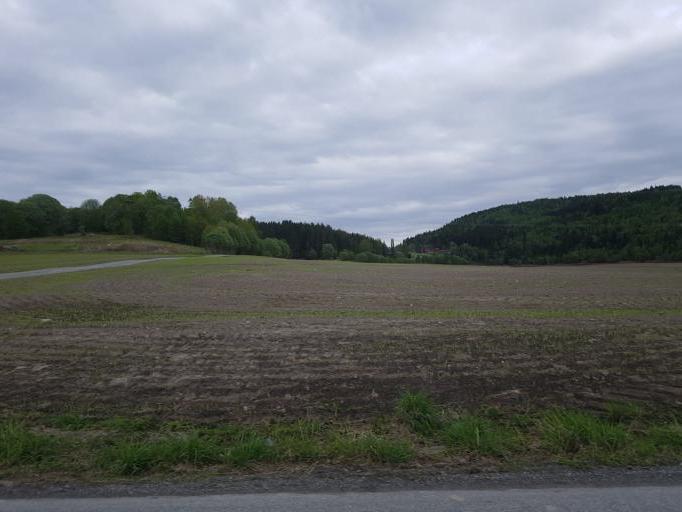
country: NO
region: Nord-Trondelag
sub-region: Levanger
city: Levanger
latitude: 63.7199
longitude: 11.2562
